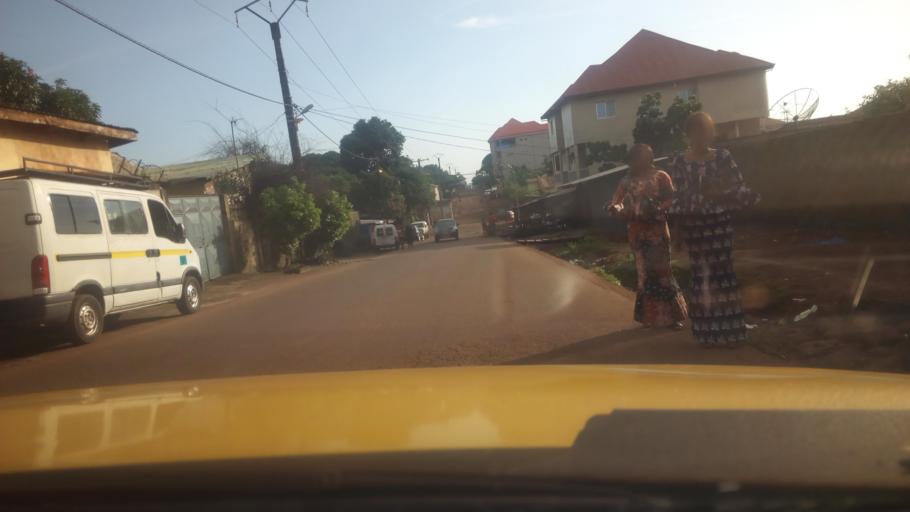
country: GN
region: Conakry
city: Conakry
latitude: 9.6187
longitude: -13.6089
